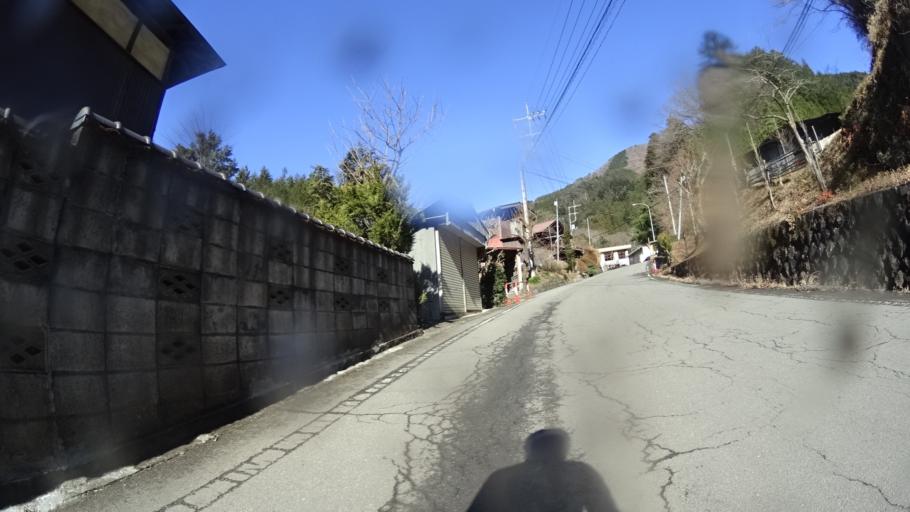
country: JP
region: Yamanashi
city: Uenohara
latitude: 35.7012
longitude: 139.0231
